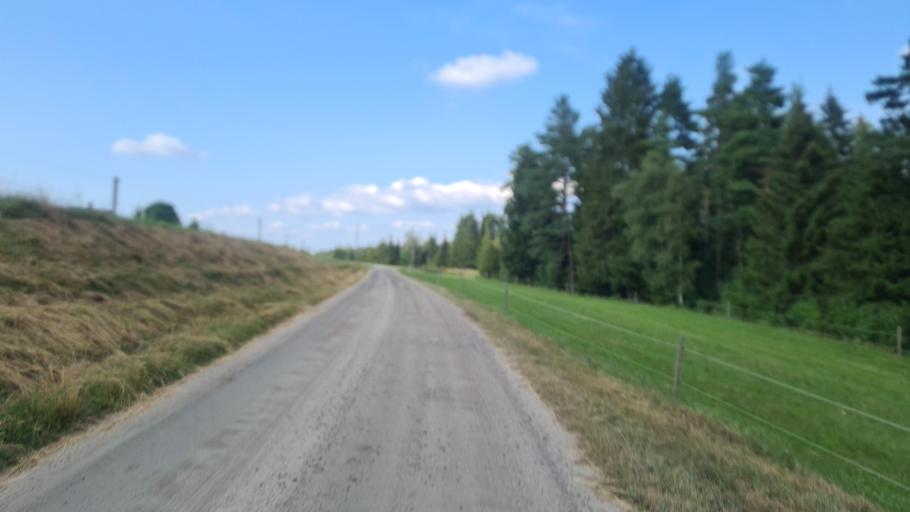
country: SE
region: Kronoberg
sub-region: Ljungby Kommun
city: Ljungby
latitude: 56.7196
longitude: 13.8811
